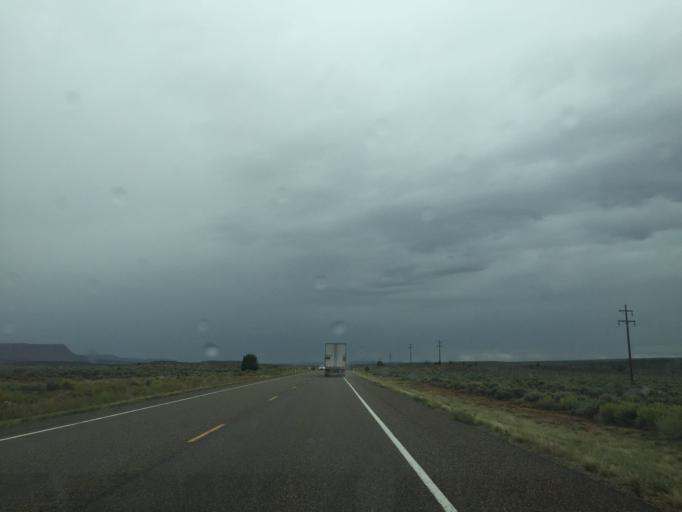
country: US
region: Utah
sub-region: Kane County
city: Kanab
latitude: 37.1188
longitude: -112.1061
